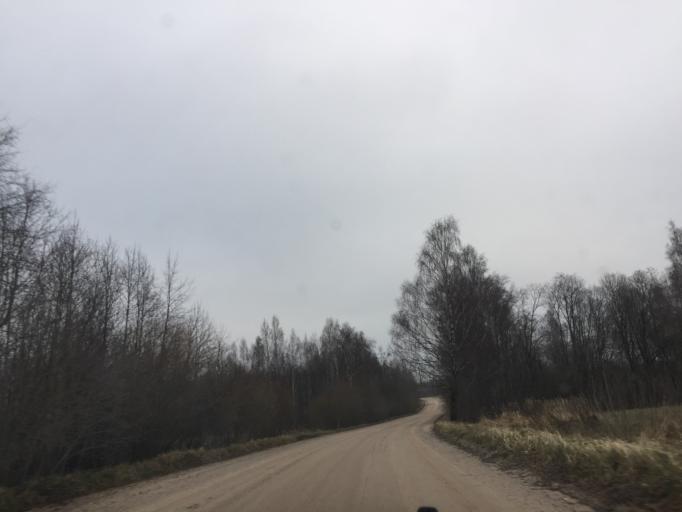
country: LV
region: Limbazu Rajons
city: Limbazi
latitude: 57.5882
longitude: 24.5138
